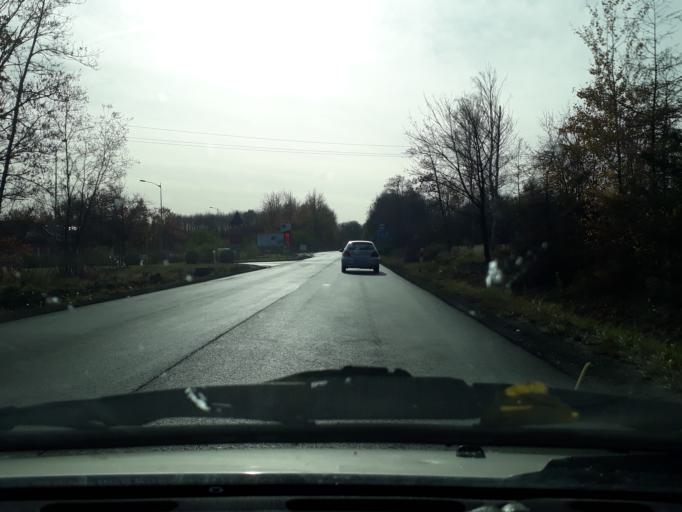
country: PL
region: Silesian Voivodeship
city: Miasteczko Slaskie
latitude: 50.5009
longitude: 18.9387
